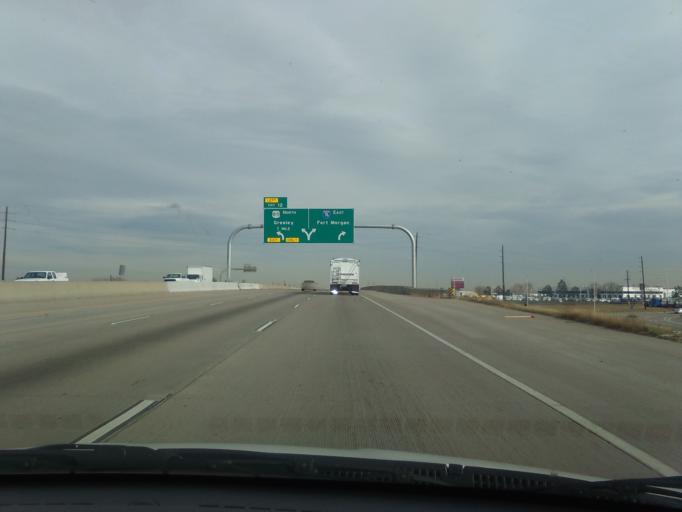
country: US
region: Colorado
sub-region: Adams County
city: Derby
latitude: 39.8695
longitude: -104.9026
